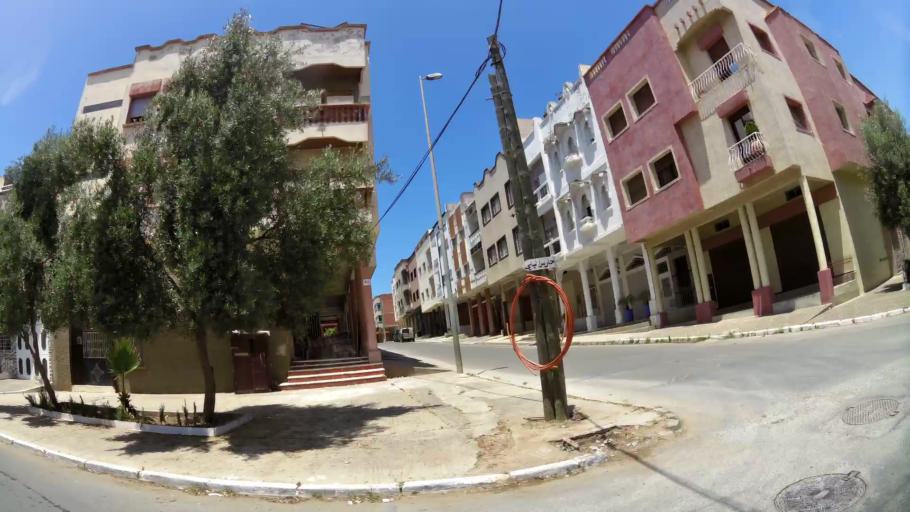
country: MA
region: Gharb-Chrarda-Beni Hssen
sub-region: Kenitra Province
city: Kenitra
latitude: 34.2522
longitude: -6.6173
